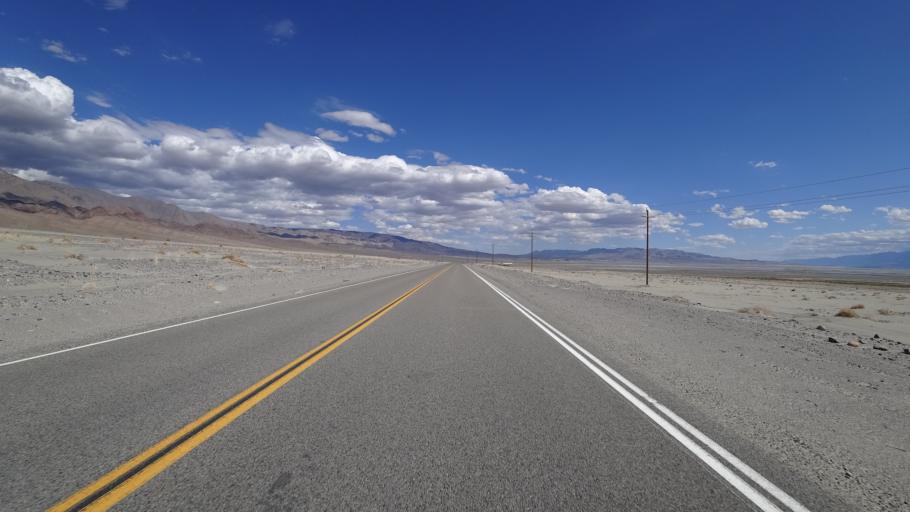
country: US
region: California
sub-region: Inyo County
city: Lone Pine
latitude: 36.5091
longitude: -117.8920
